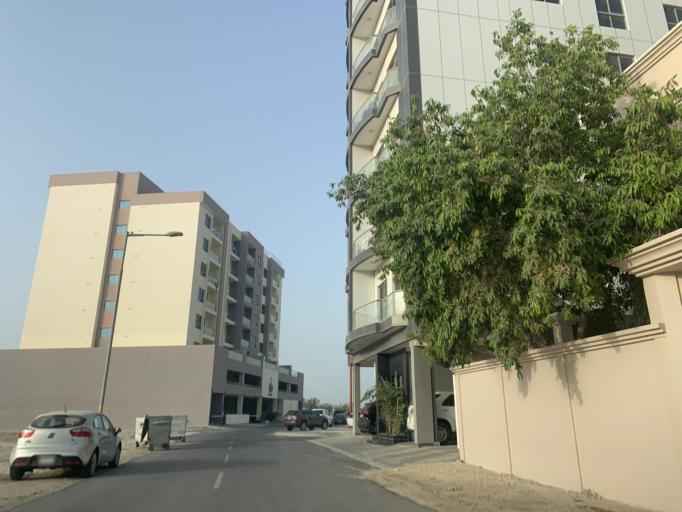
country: BH
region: Manama
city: Jidd Hafs
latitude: 26.2412
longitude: 50.5320
